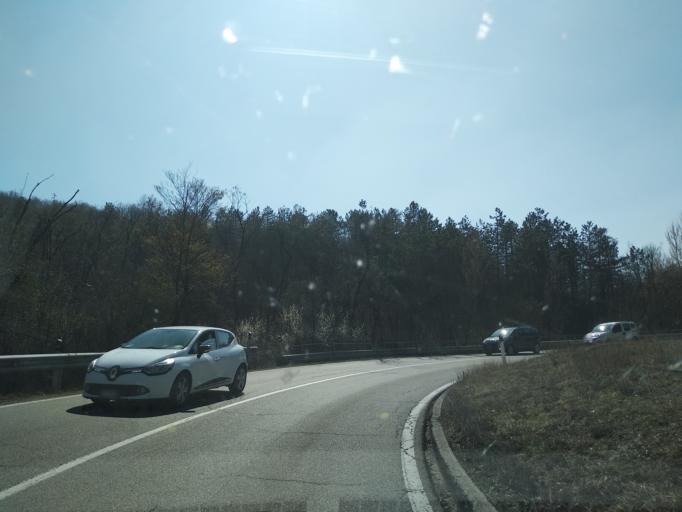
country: IT
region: Emilia-Romagna
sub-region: Provincia di Reggio Emilia
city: Vezzano sul Crostolo
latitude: 44.5820
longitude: 10.5339
